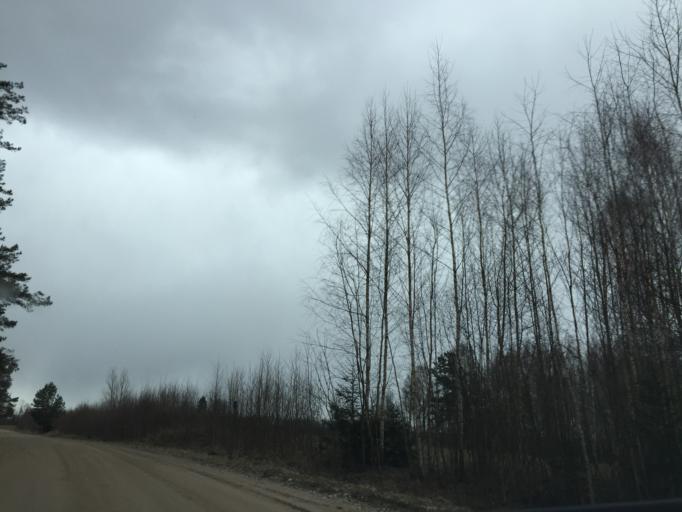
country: LV
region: Varkava
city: Vecvarkava
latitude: 56.0656
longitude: 26.5344
